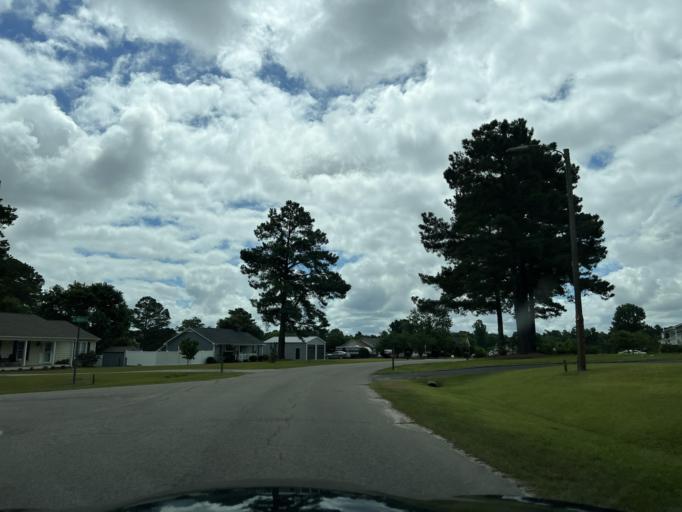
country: US
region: North Carolina
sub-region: Lee County
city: Sanford
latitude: 35.4340
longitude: -79.1624
